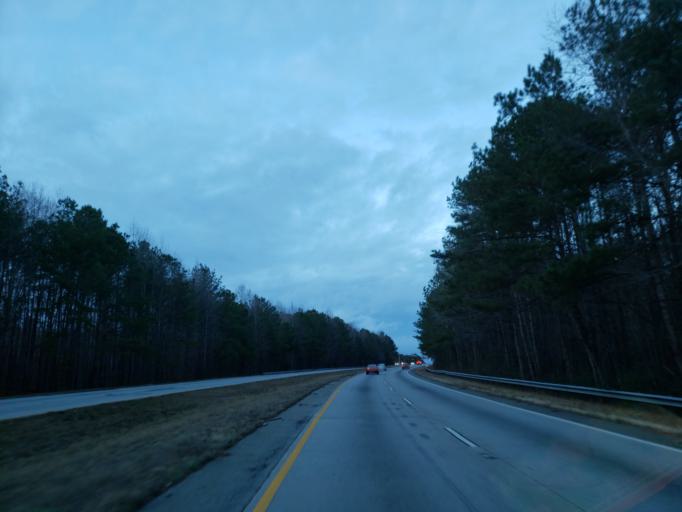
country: US
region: Georgia
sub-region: Fulton County
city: Union City
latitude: 33.6952
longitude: -84.5766
